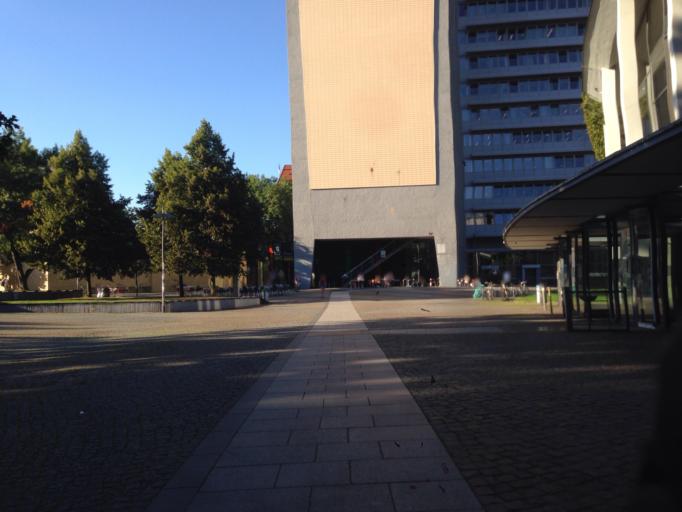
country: DE
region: Hamburg
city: Eimsbuettel
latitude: 53.5663
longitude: 9.9850
